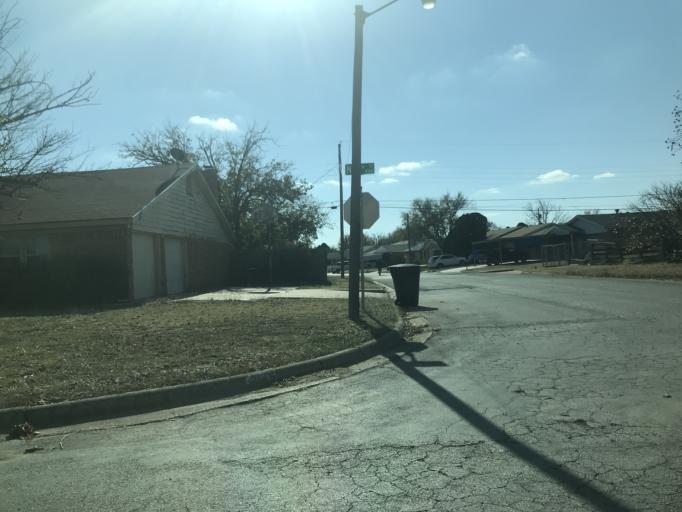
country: US
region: Texas
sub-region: Taylor County
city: Abilene
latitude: 32.4579
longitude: -99.7812
